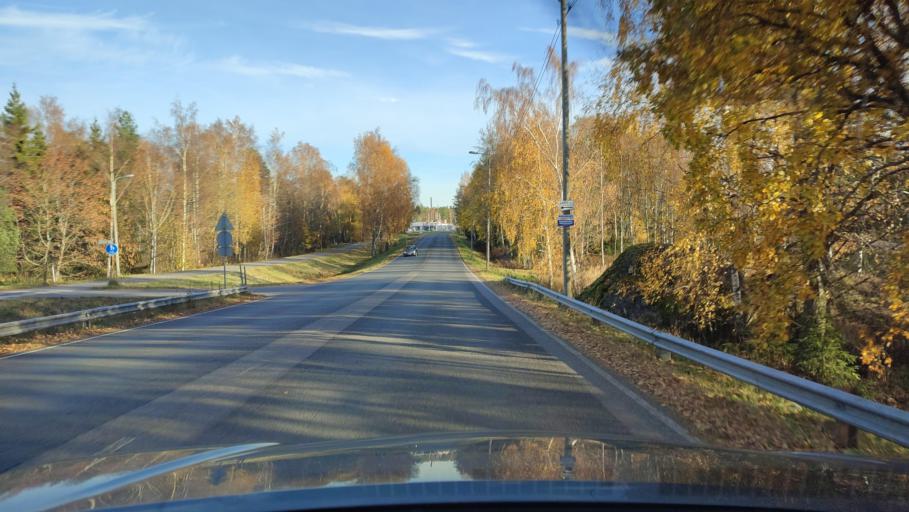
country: FI
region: Ostrobothnia
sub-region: Vaasa
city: Vaasa
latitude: 63.0803
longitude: 21.6522
